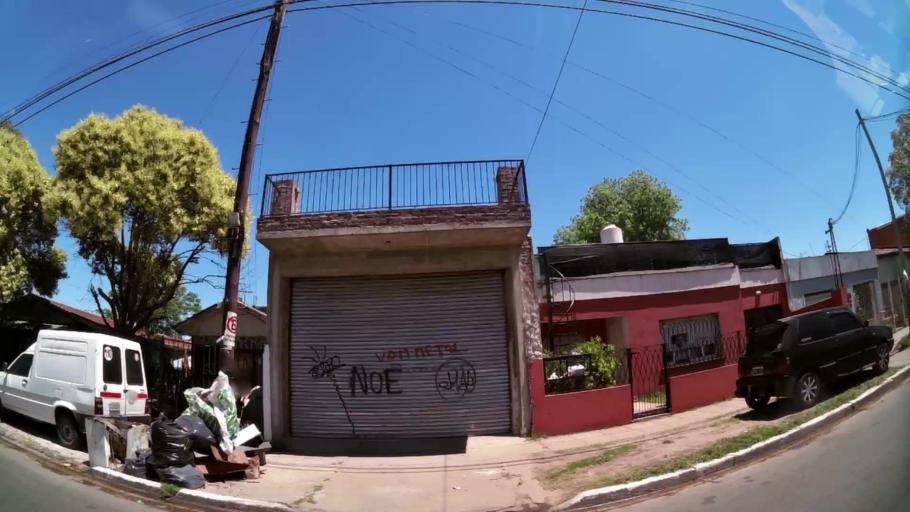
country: AR
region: Buenos Aires
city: Hurlingham
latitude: -34.5086
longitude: -58.6740
